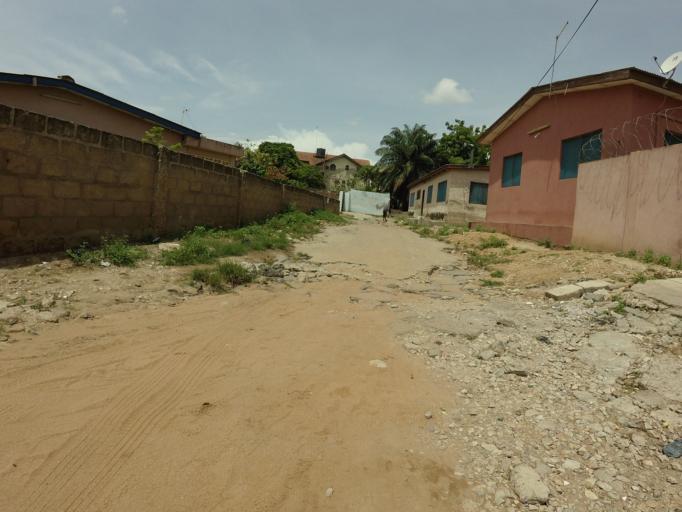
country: GH
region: Greater Accra
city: Dome
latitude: 5.6115
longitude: -0.2359
